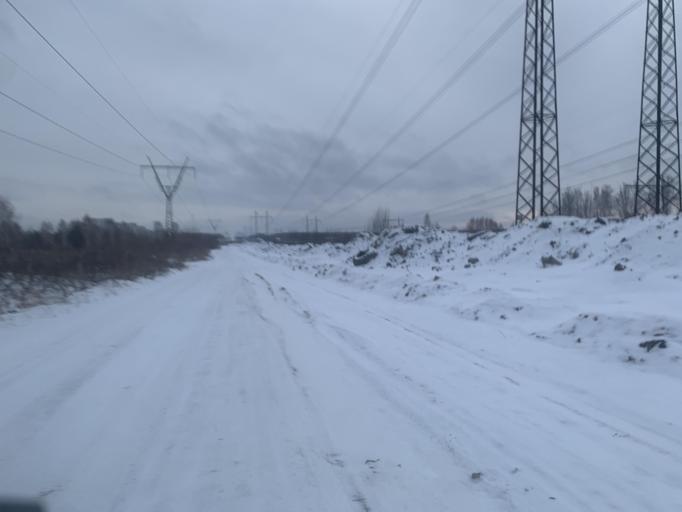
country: RU
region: Chelyabinsk
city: Roshchino
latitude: 55.1893
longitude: 61.2585
